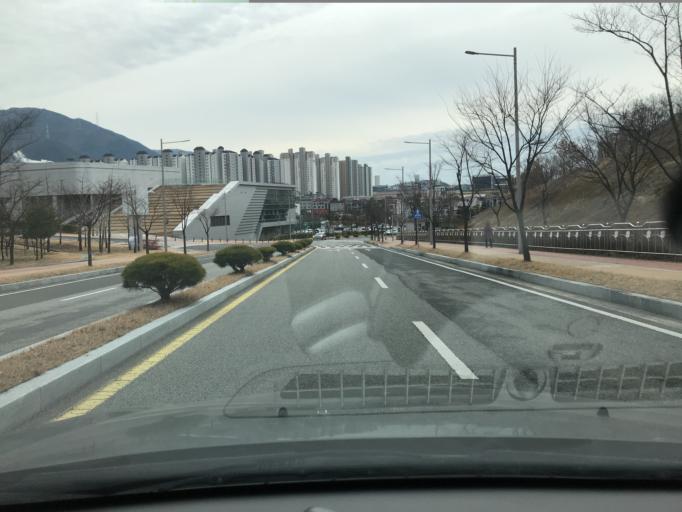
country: KR
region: Daegu
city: Hwawon
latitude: 35.7024
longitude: 128.4582
